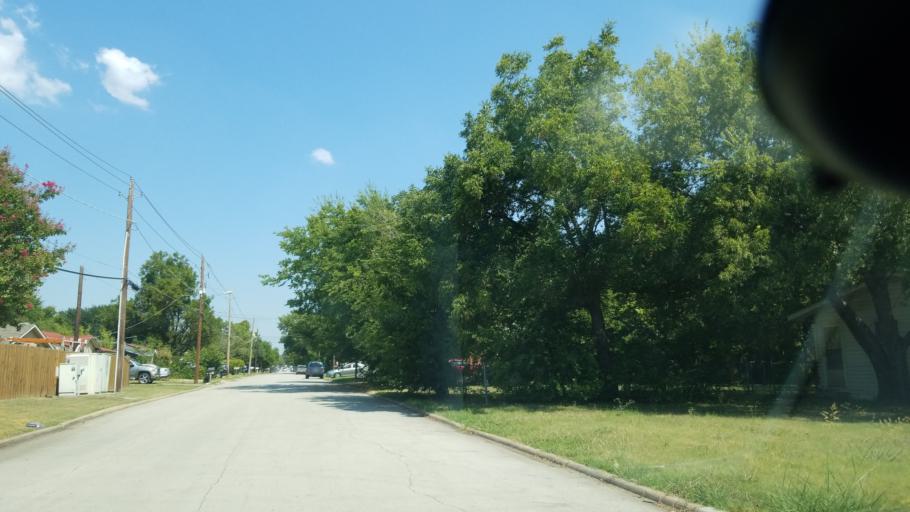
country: US
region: Texas
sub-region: Dallas County
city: Grand Prairie
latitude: 32.7105
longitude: -96.9844
